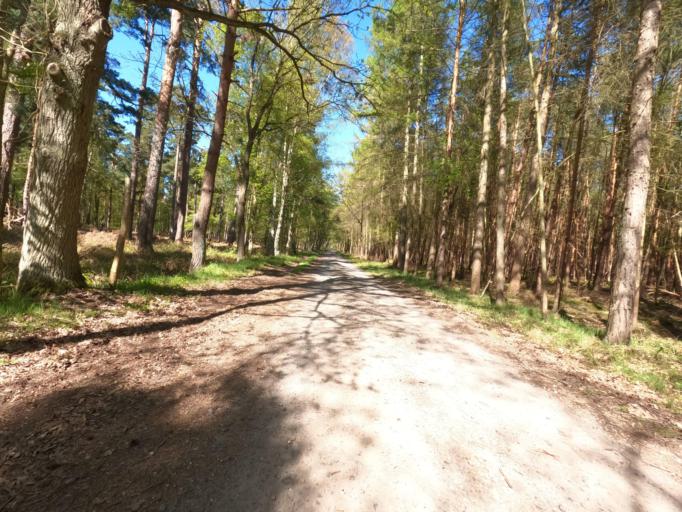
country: DE
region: Mecklenburg-Vorpommern
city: Born
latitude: 54.4003
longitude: 12.5268
